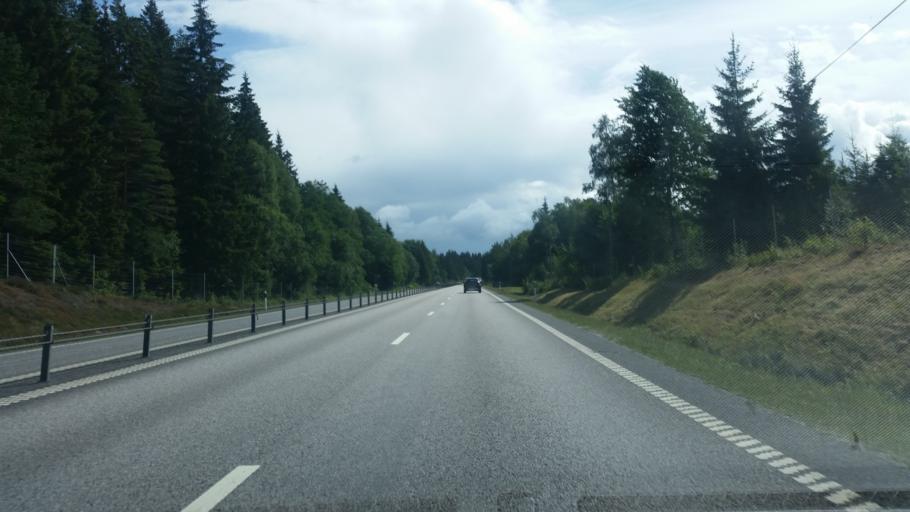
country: SE
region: Joenkoeping
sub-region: Mullsjo Kommun
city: Mullsjoe
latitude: 57.7738
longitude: 13.6971
